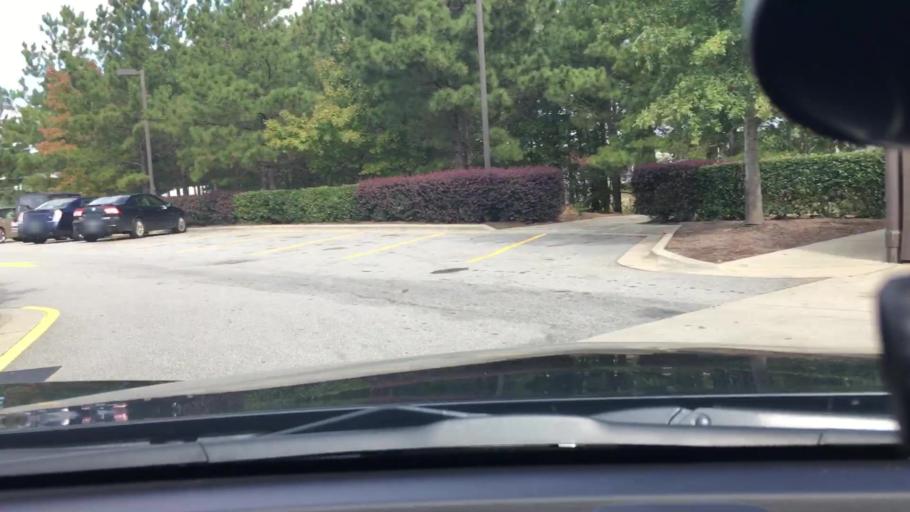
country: US
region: North Carolina
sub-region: Wake County
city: Apex
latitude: 35.7058
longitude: -78.8348
